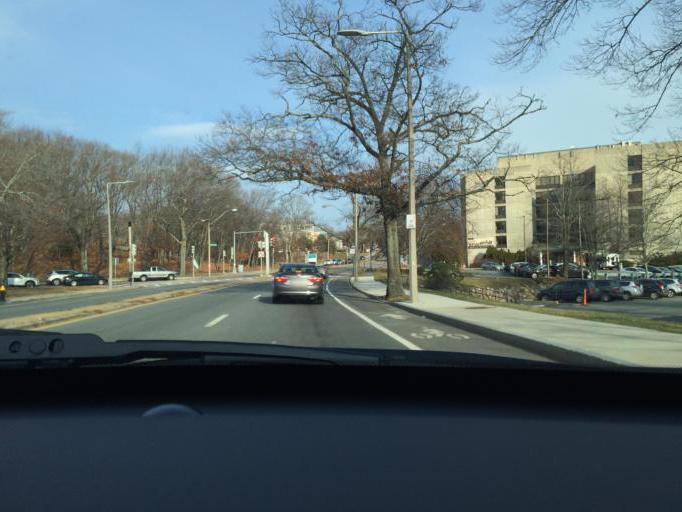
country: US
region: Massachusetts
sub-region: Suffolk County
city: Jamaica Plain
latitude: 42.2963
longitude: -71.1337
